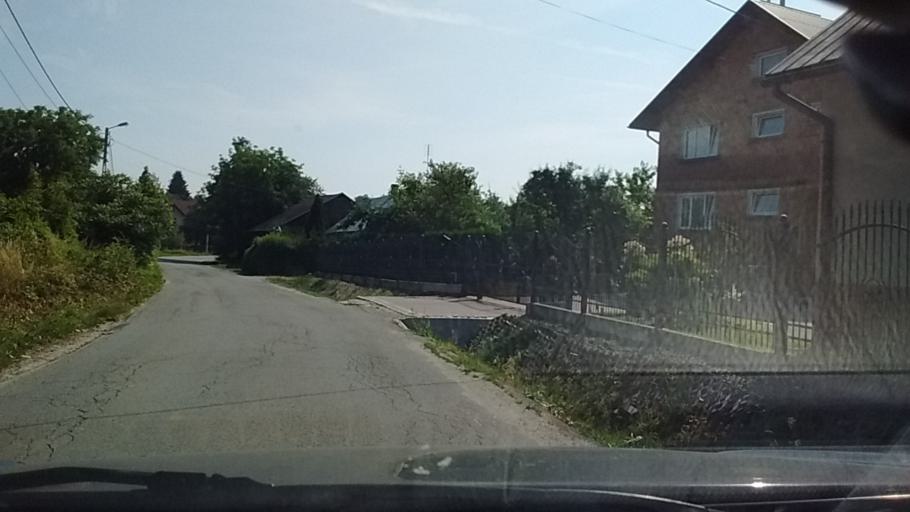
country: PL
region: Subcarpathian Voivodeship
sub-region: Powiat lancucki
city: Wysoka
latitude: 50.0427
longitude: 22.2540
